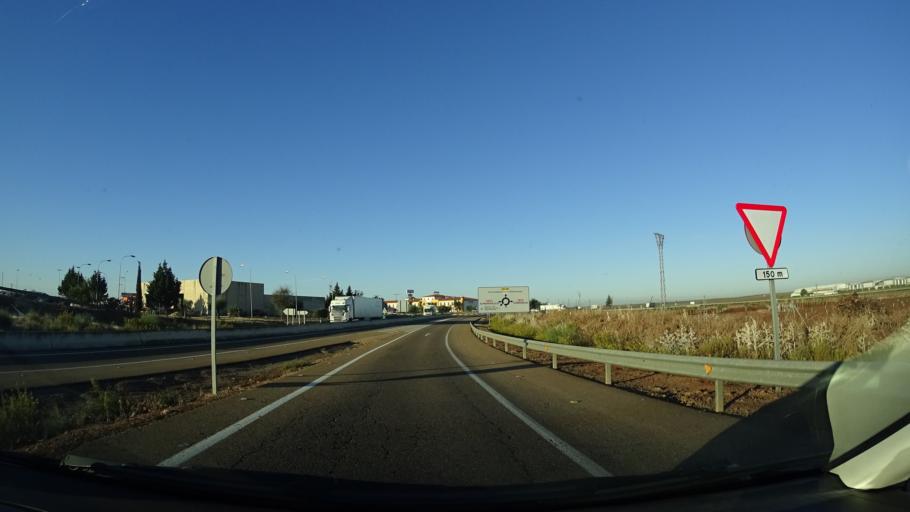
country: ES
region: Extremadura
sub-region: Provincia de Badajoz
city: Almendralejo
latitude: 38.7113
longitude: -6.3974
